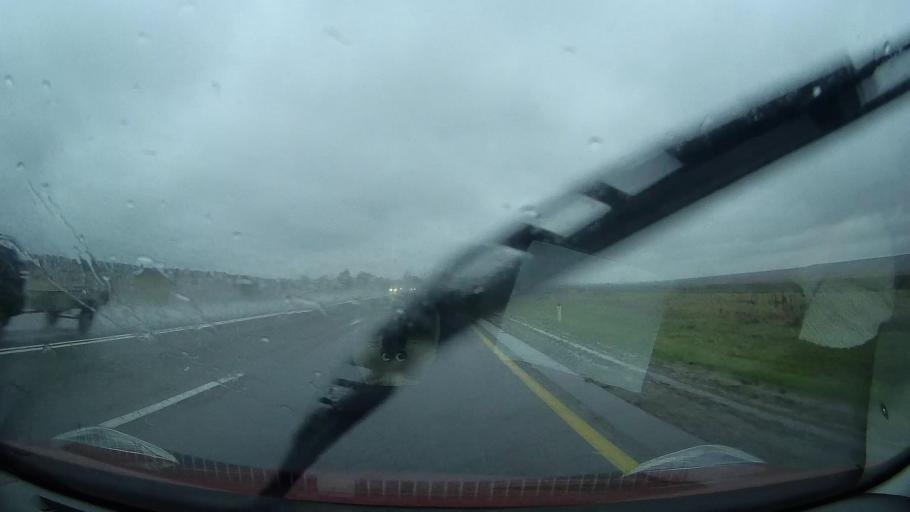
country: RU
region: Stavropol'skiy
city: Nevinnomyssk
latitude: 44.6290
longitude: 42.0379
